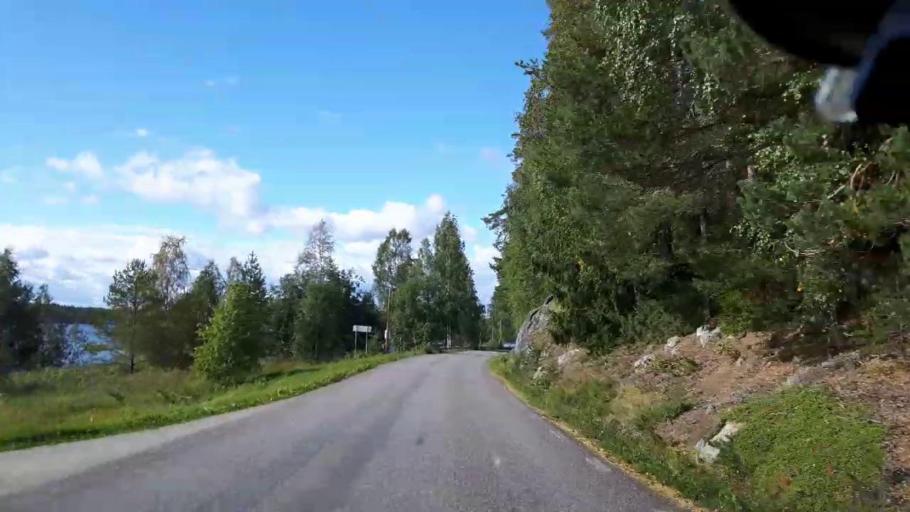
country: SE
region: Jaemtland
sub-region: Braecke Kommun
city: Braecke
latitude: 63.1727
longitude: 15.5673
